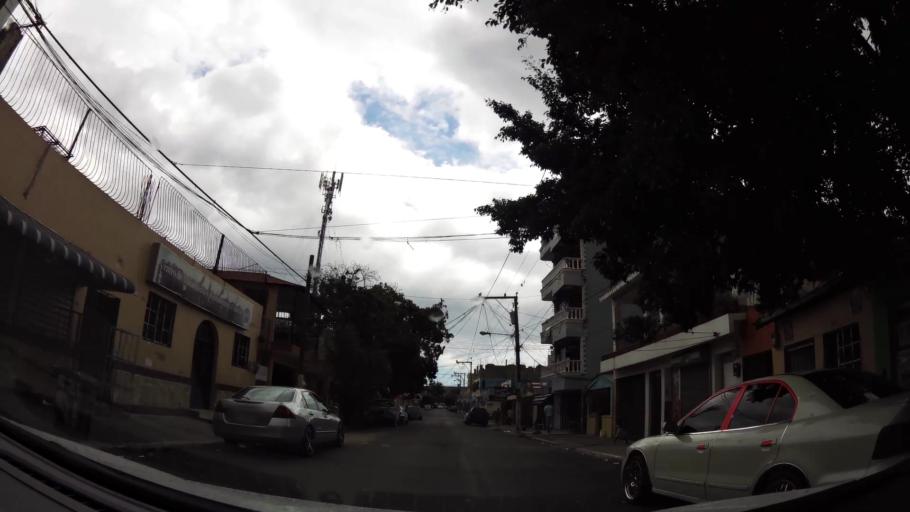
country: DO
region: Nacional
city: San Carlos
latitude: 18.4880
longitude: -69.9110
